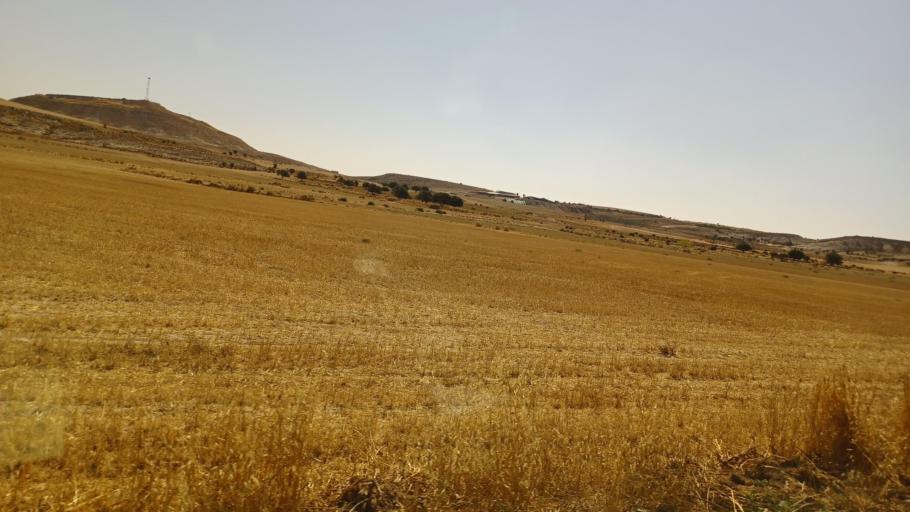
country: CY
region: Larnaka
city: Athienou
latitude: 35.0314
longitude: 33.5128
